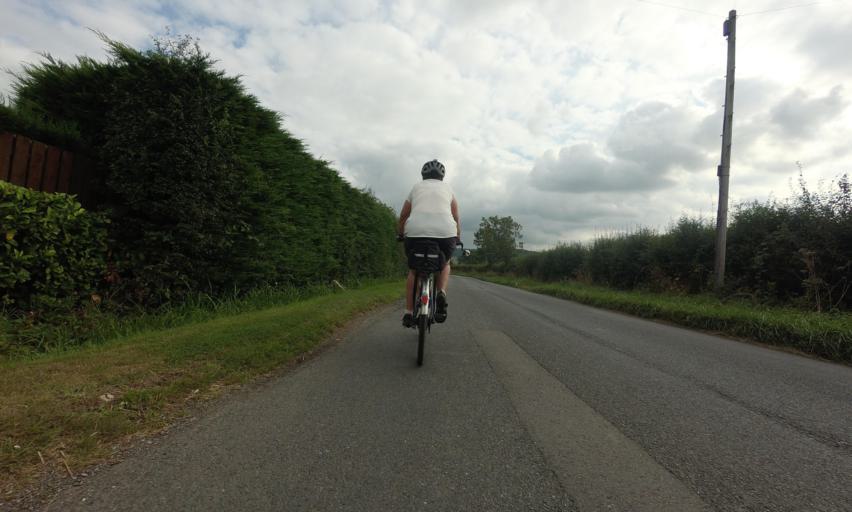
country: GB
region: England
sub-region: Gloucestershire
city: Winchcombe
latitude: 51.9875
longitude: -1.9994
